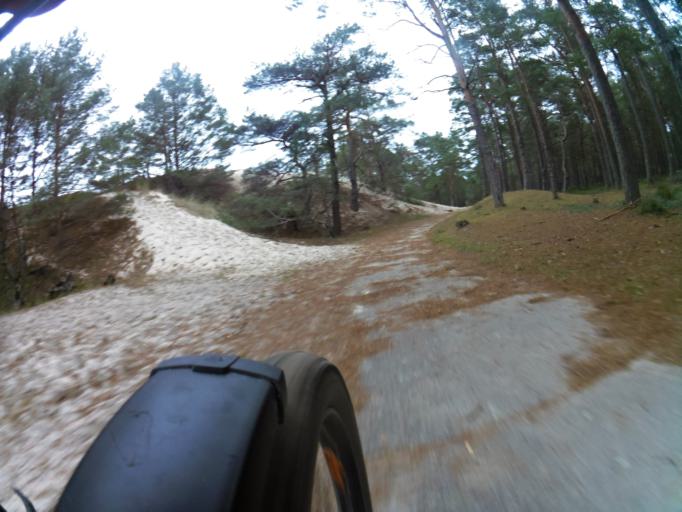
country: PL
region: Pomeranian Voivodeship
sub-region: Powiat wejherowski
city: Choczewo
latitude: 54.7820
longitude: 17.7302
